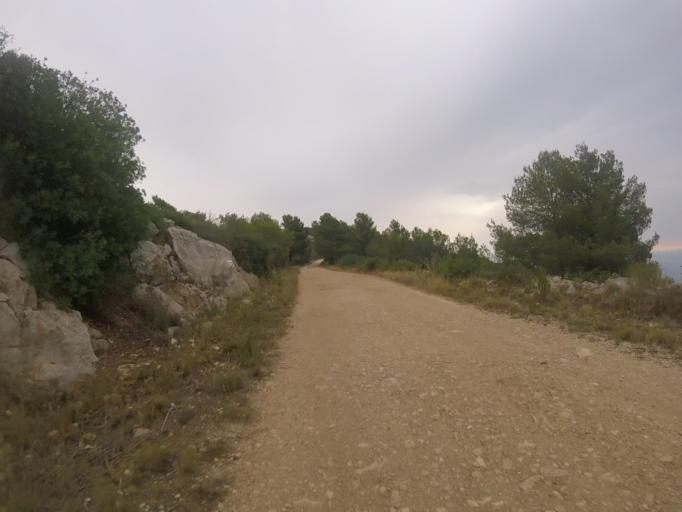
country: ES
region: Valencia
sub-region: Provincia de Castello
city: Alcoceber
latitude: 40.2732
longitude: 0.2781
